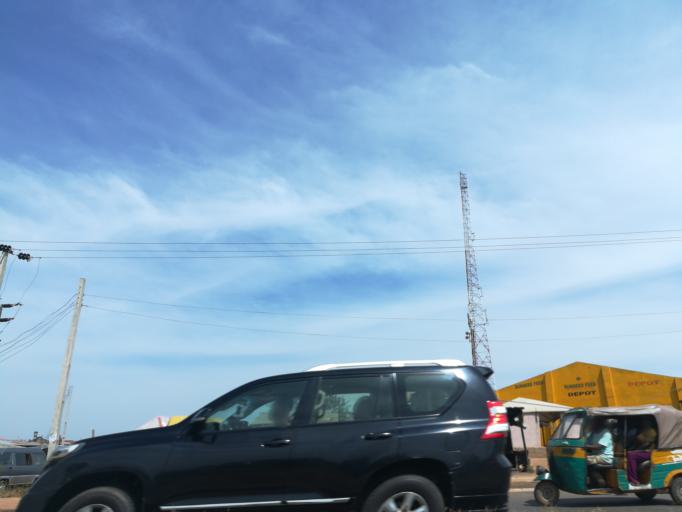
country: NG
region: Plateau
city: Bukuru
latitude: 9.7837
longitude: 8.8595
